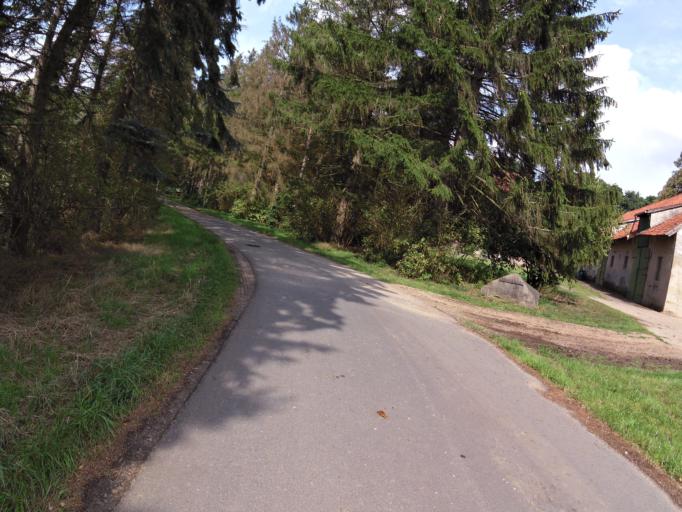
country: DE
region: Lower Saxony
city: Hilgermissen
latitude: 52.8833
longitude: 9.1782
